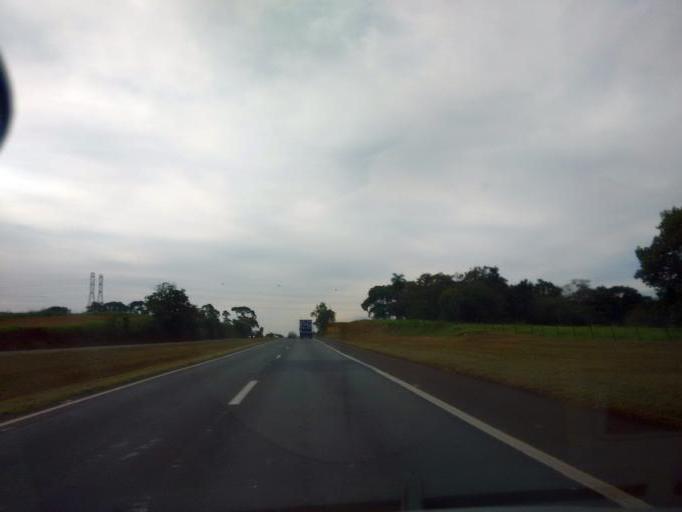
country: BR
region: Sao Paulo
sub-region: Araraquara
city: Araraquara
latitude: -21.7928
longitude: -48.2132
